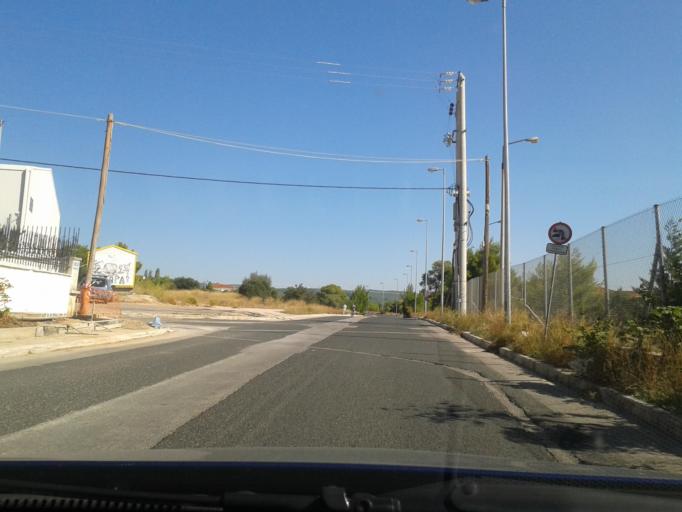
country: GR
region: Attica
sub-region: Nomarchia Anatolikis Attikis
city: Thrakomakedones
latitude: 38.1221
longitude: 23.7642
